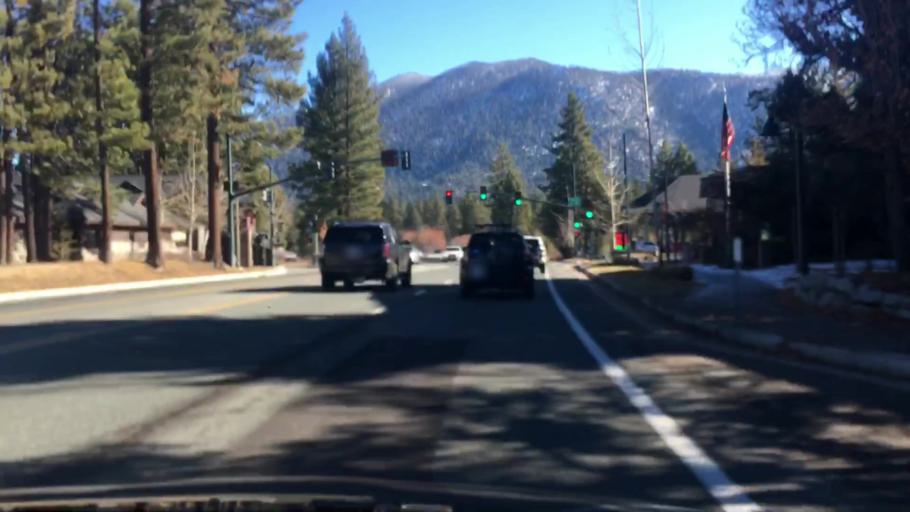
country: US
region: California
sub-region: El Dorado County
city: South Lake Tahoe
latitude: 38.9457
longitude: -119.9694
